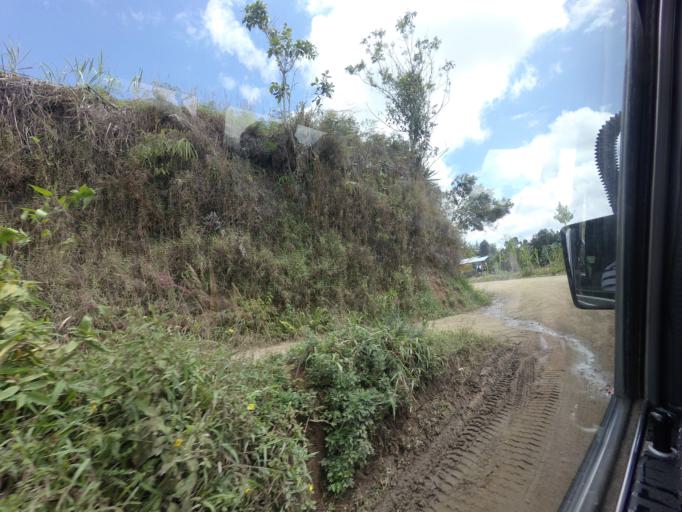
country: CO
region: Huila
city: Isnos
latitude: 1.9443
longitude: -76.2753
